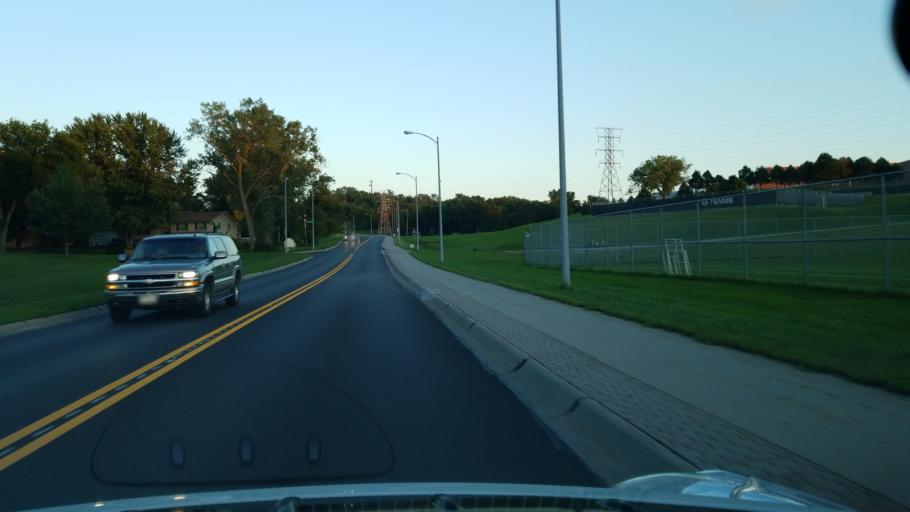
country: US
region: Nebraska
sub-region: Sarpy County
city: Bellevue
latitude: 41.1498
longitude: -95.9050
